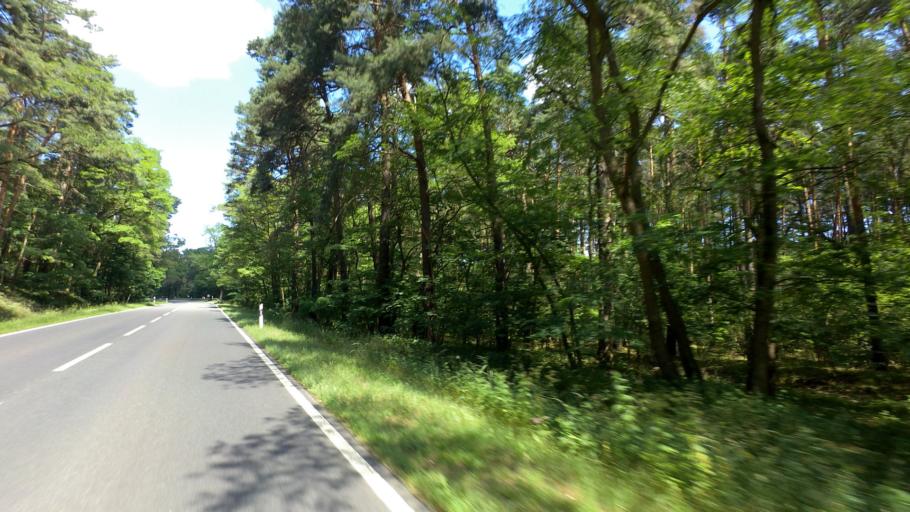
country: DE
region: Brandenburg
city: Golssen
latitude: 51.9998
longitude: 13.5589
